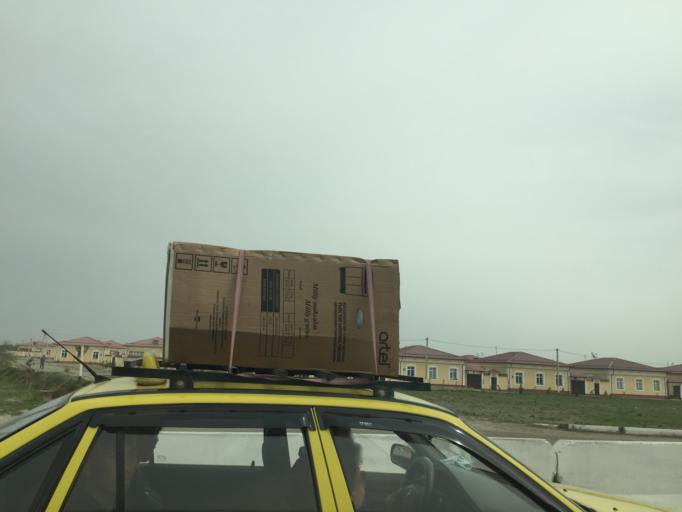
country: UZ
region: Bukhara
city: Kogon
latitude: 39.7352
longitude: 64.5060
